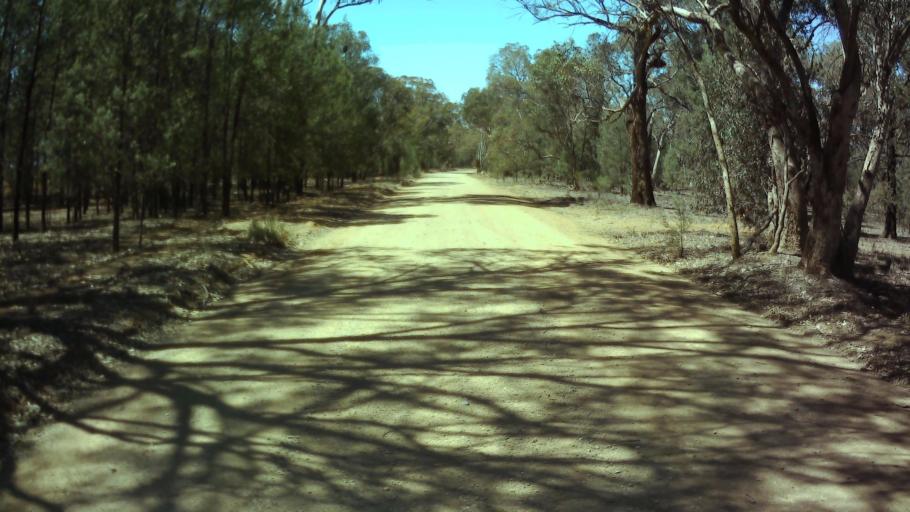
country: AU
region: New South Wales
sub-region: Weddin
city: Grenfell
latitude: -33.8603
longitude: 148.0871
